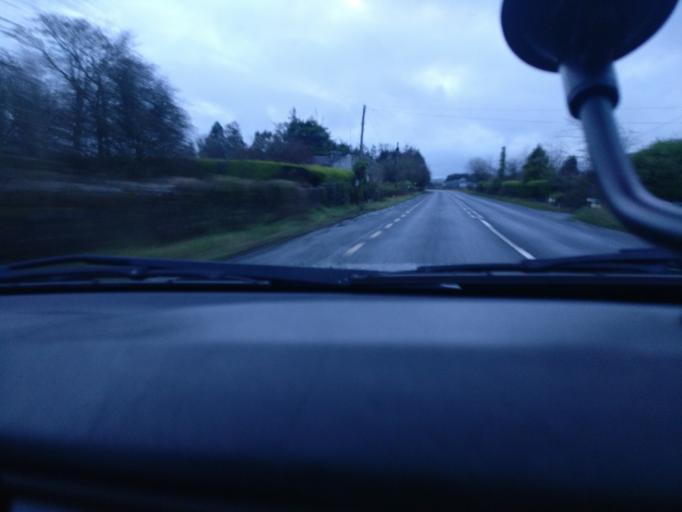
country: IE
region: Connaught
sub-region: County Galway
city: Loughrea
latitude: 53.2444
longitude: -8.4484
